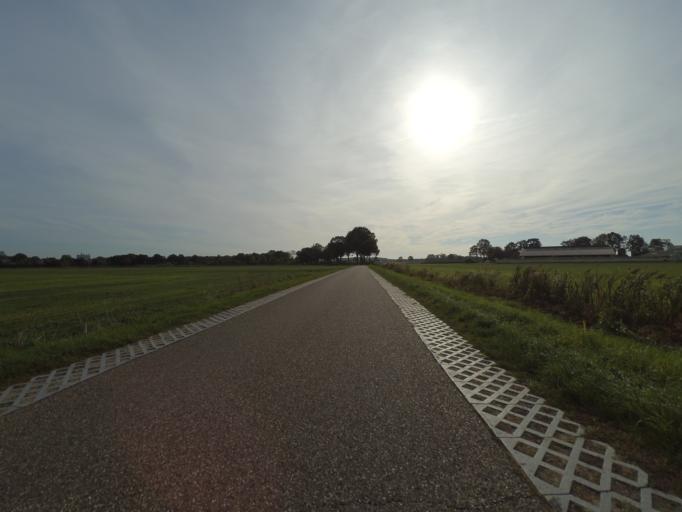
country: NL
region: Overijssel
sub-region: Gemeente Raalte
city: Raalte
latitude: 52.3609
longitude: 6.3665
